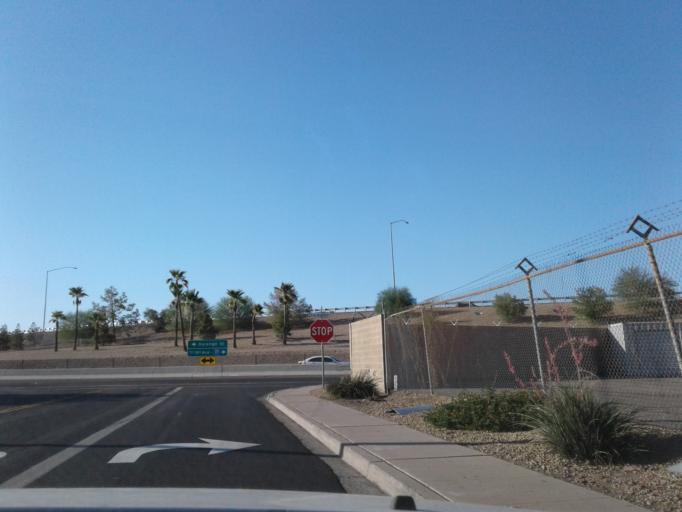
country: US
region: Arizona
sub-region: Maricopa County
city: Phoenix
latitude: 33.4287
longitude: -112.1063
